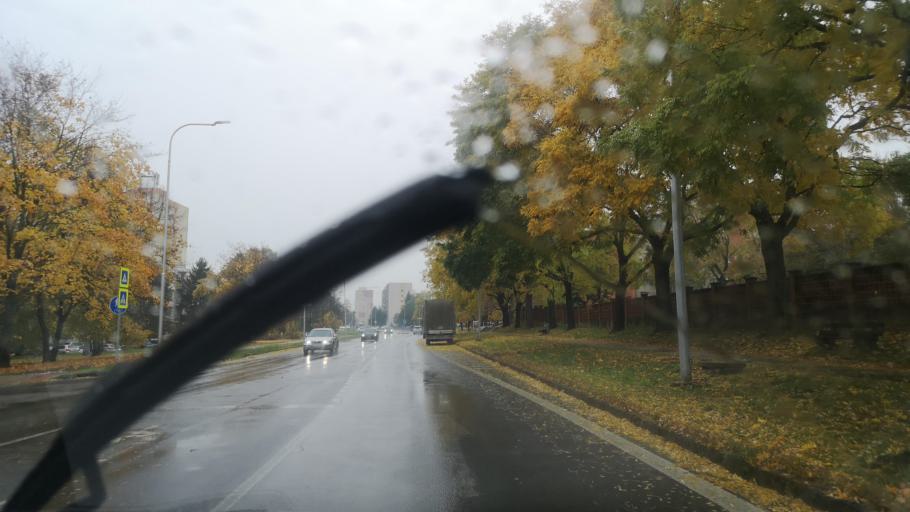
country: SK
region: Nitriansky
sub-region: Okres Nitra
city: Nitra
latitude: 48.3107
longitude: 18.1129
